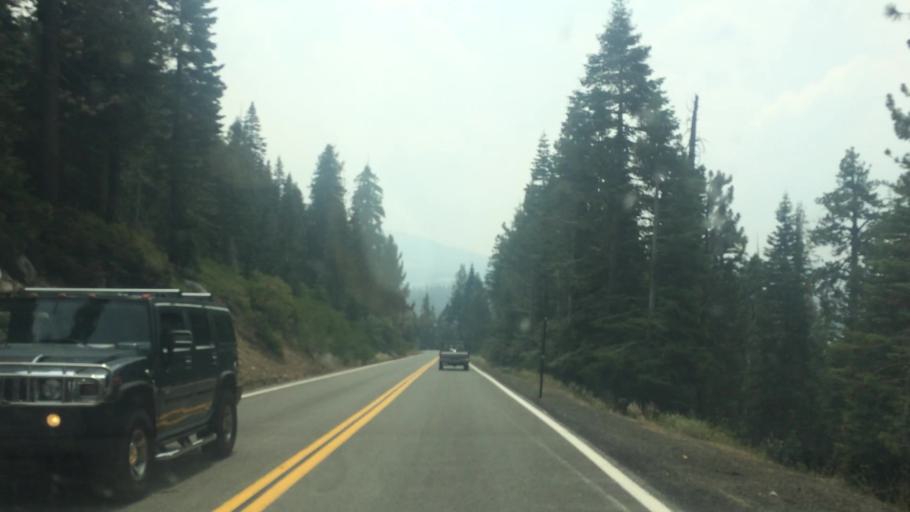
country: US
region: California
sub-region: El Dorado County
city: South Lake Tahoe
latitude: 38.6892
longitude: -120.1240
